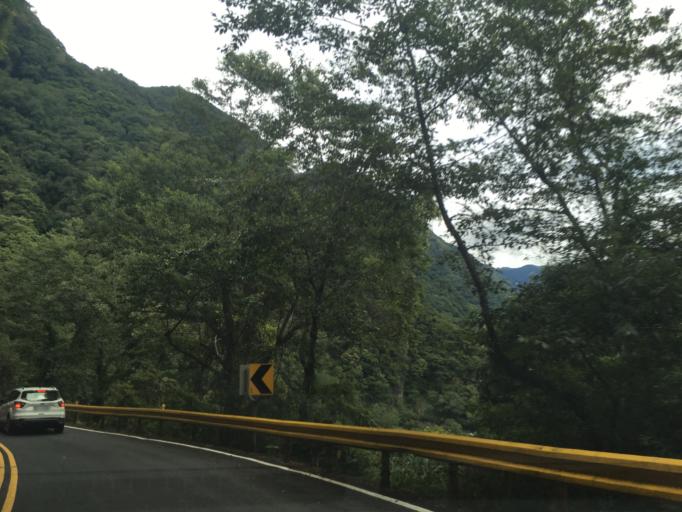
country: TW
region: Taiwan
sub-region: Hualien
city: Hualian
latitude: 24.2020
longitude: 121.4286
